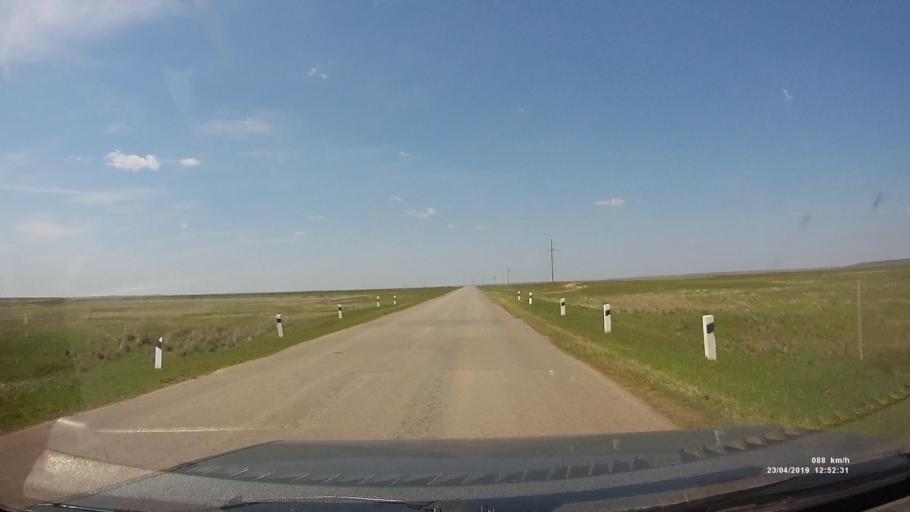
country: RU
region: Kalmykiya
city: Yashalta
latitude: 46.5654
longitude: 42.6084
